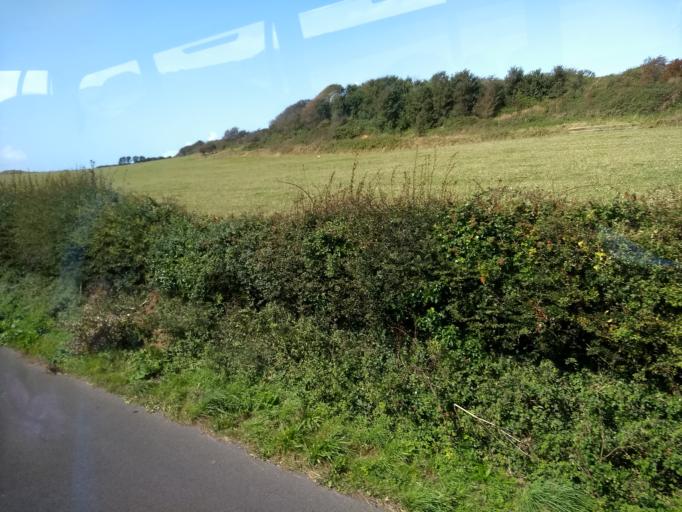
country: GB
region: England
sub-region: Isle of Wight
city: Totland
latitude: 50.6719
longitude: -1.5506
